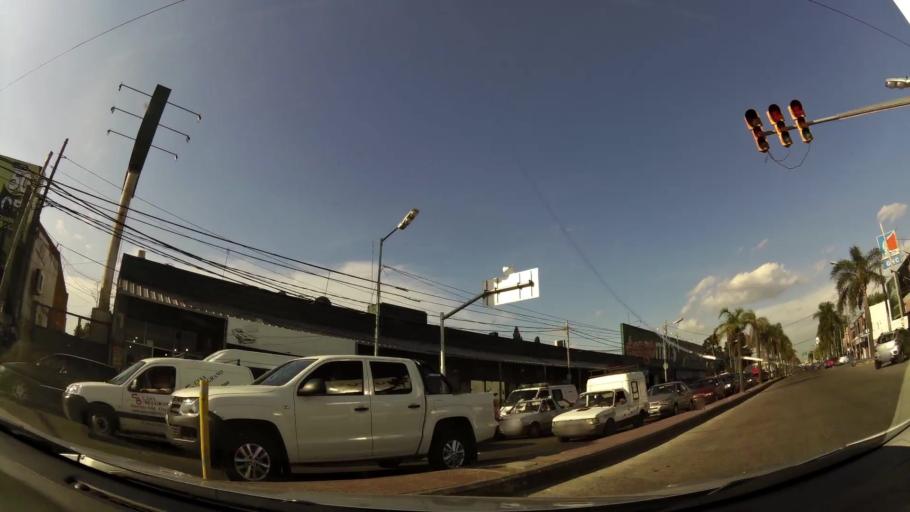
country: AR
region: Buenos Aires
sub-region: Partido de Tigre
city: Tigre
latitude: -34.4752
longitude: -58.6619
